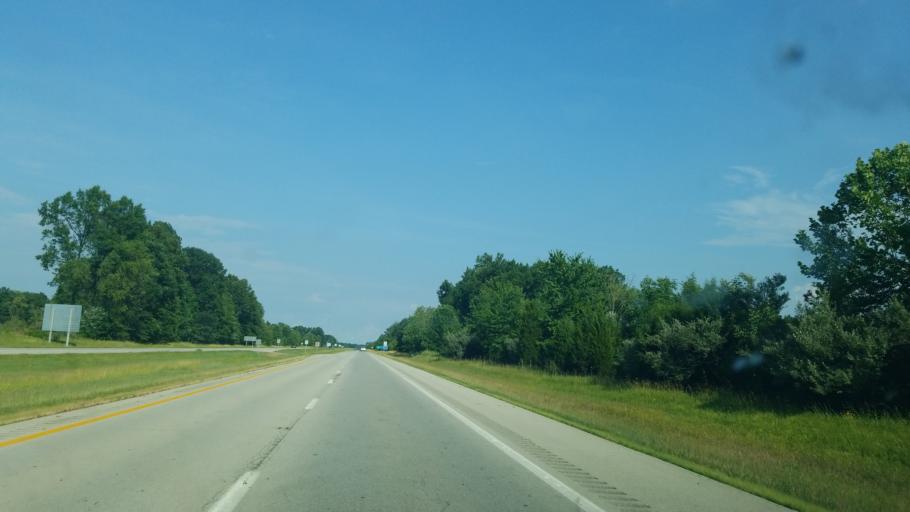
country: US
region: Ohio
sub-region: Brown County
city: Mount Orab
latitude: 39.0389
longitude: -83.9124
